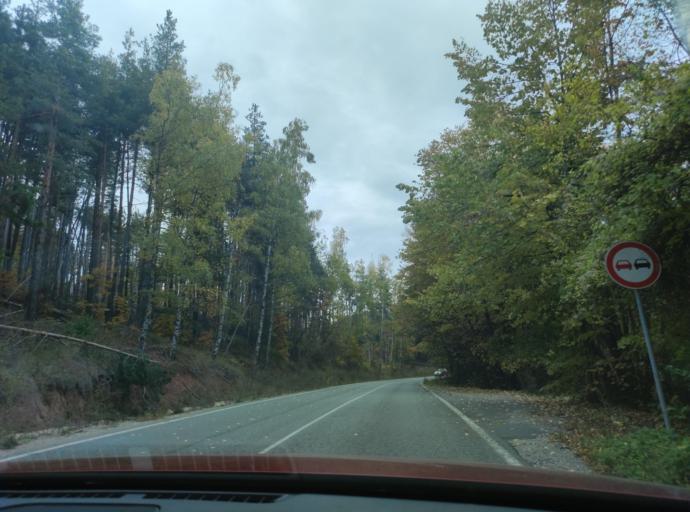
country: BG
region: Sofiya
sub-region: Obshtina Godech
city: Godech
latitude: 43.0171
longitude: 23.1202
